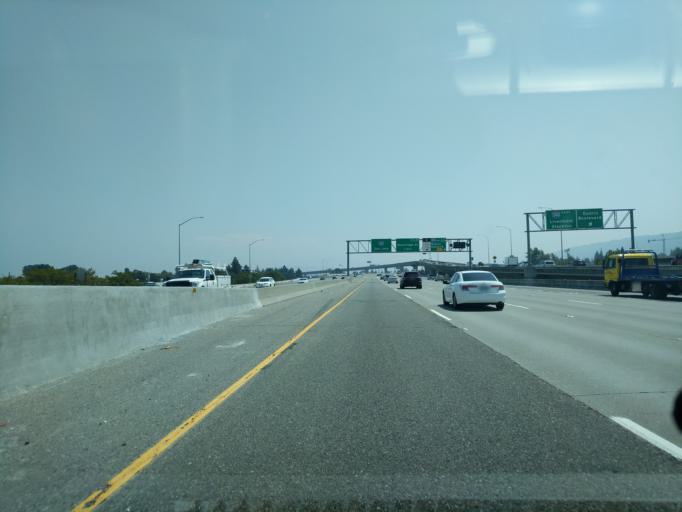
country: US
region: California
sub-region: Alameda County
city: Dublin
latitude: 37.7073
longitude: -121.9269
